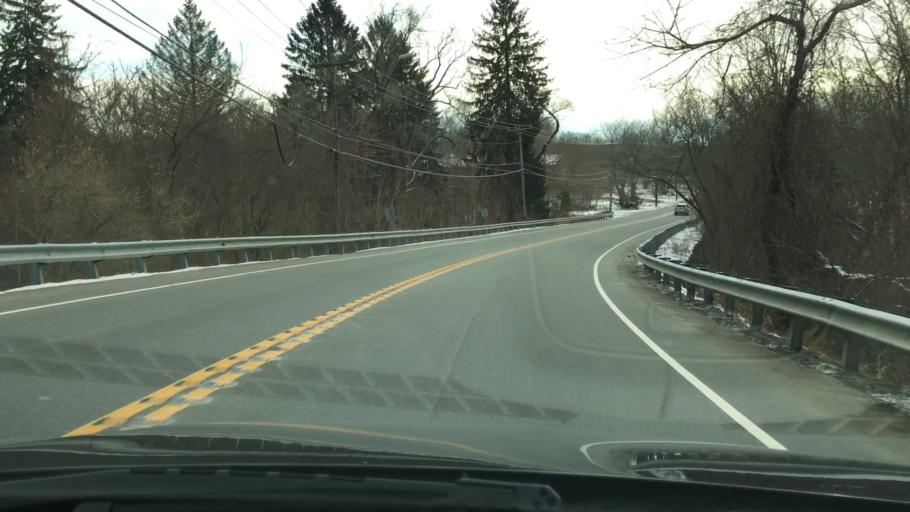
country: US
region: Connecticut
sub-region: New London County
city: Norwich
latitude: 41.4941
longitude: -72.0744
